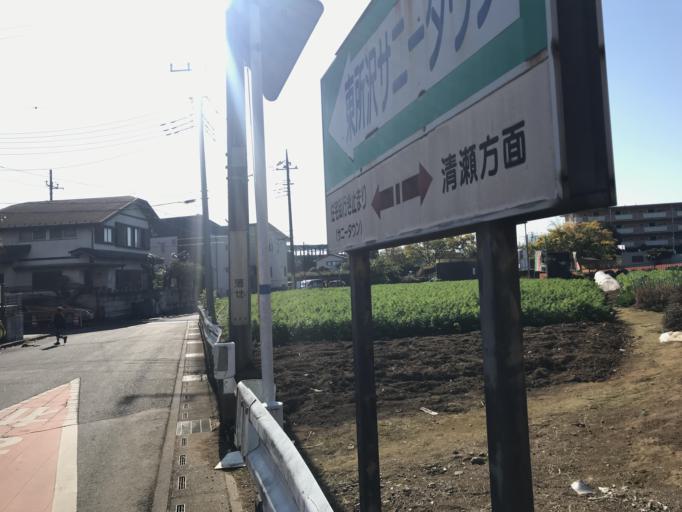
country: JP
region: Saitama
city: Tokorozawa
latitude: 35.7895
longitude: 139.5169
